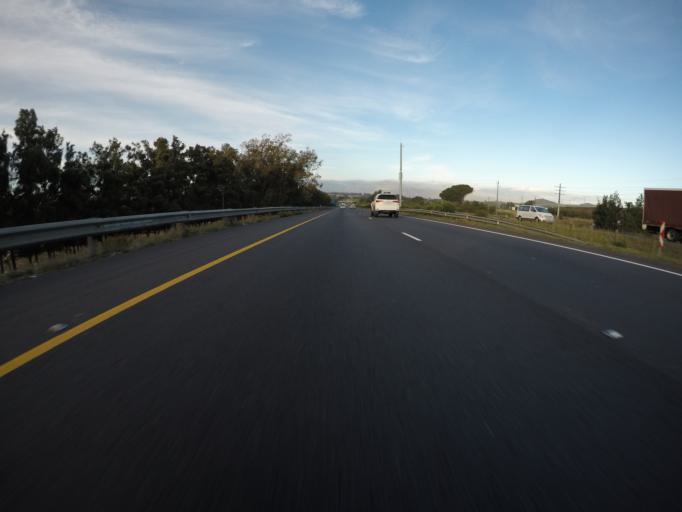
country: ZA
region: Western Cape
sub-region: Cape Winelands District Municipality
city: Stellenbosch
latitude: -33.8046
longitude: 18.8459
